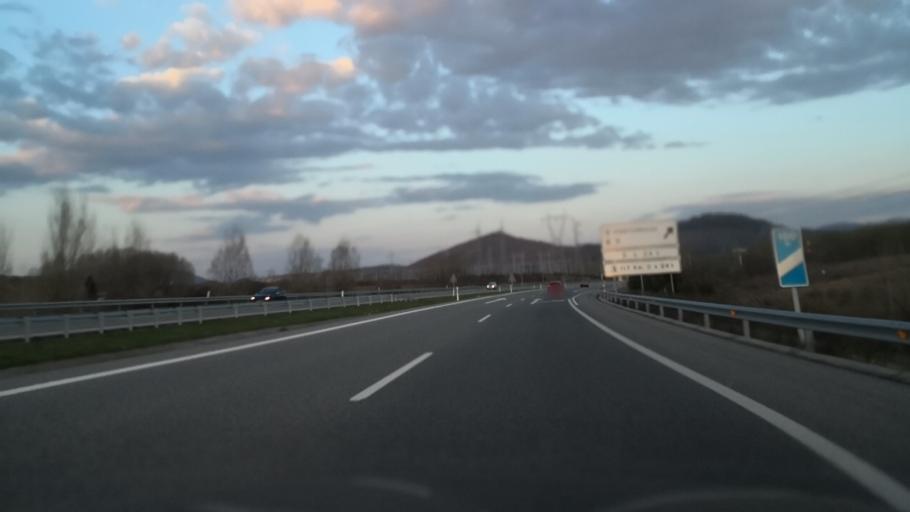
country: ES
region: Castille and Leon
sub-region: Provincia de Leon
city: Camponaraya
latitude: 42.5853
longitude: -6.6337
